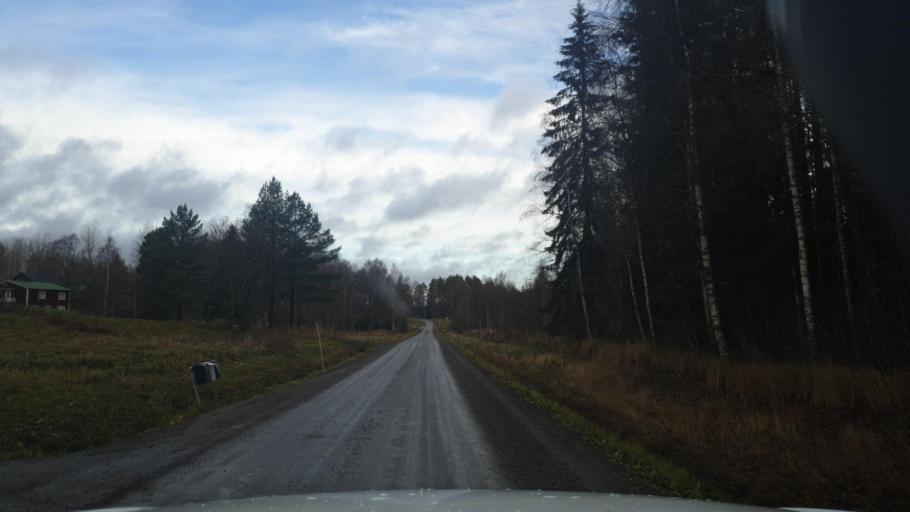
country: NO
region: Hedmark
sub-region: Eidskog
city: Skotterud
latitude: 59.8639
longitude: 11.9842
